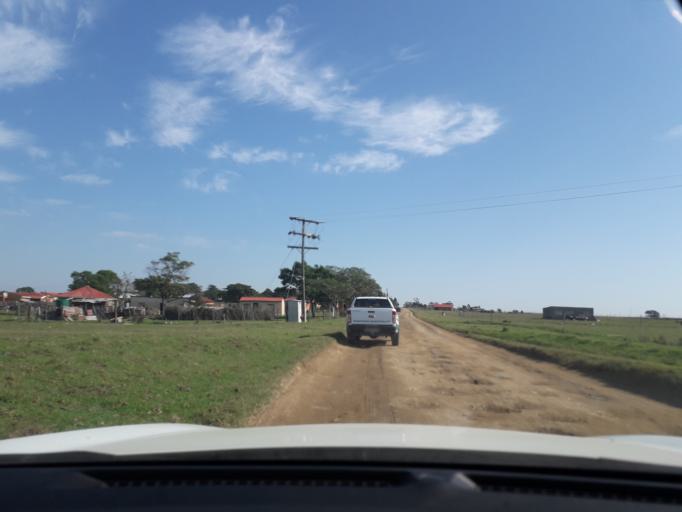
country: ZA
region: Eastern Cape
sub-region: Buffalo City Metropolitan Municipality
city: Bhisho
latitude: -32.9716
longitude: 27.3166
